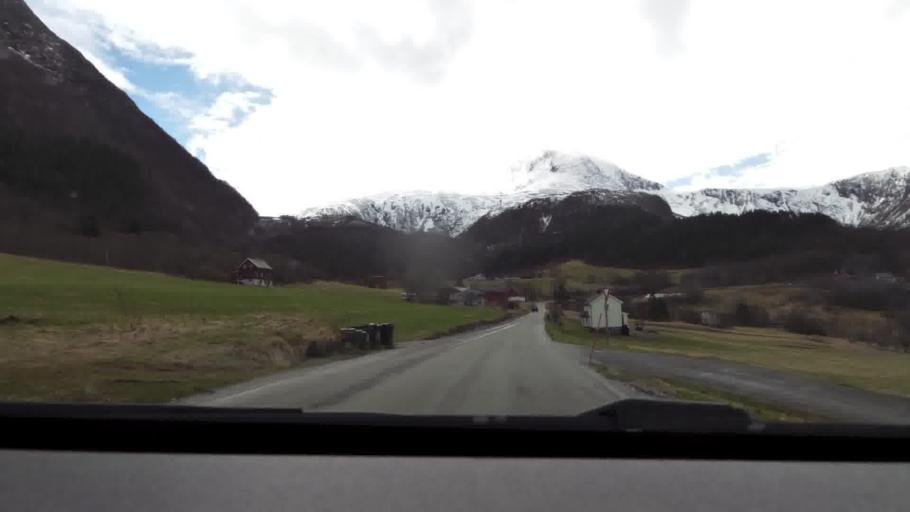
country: NO
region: More og Romsdal
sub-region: Gjemnes
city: Batnfjordsora
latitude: 62.9334
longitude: 7.6046
